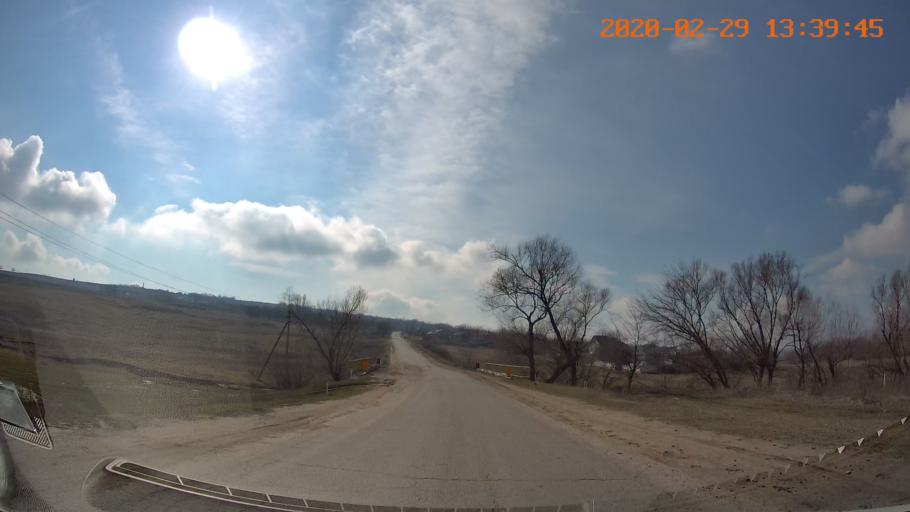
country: MD
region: Floresti
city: Leninskiy
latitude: 47.8509
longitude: 28.5762
